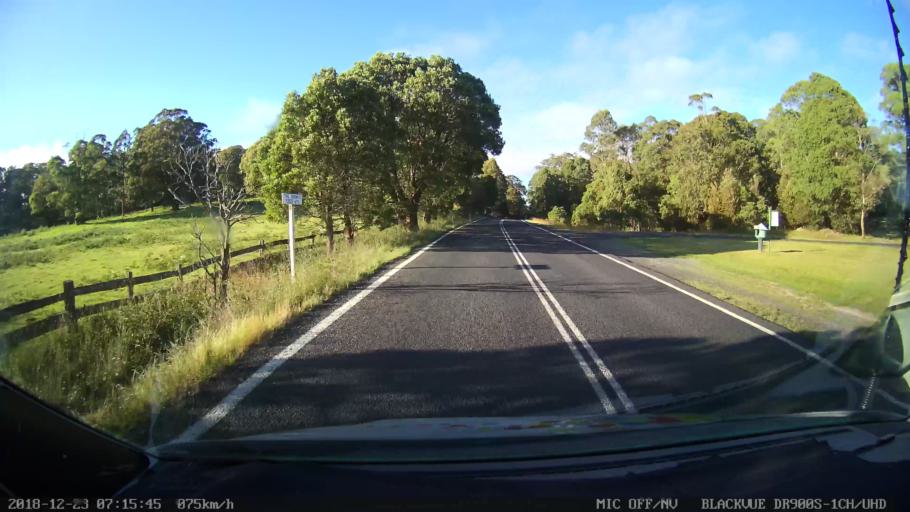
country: AU
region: New South Wales
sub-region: Bellingen
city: Dorrigo
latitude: -30.4493
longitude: 152.3151
